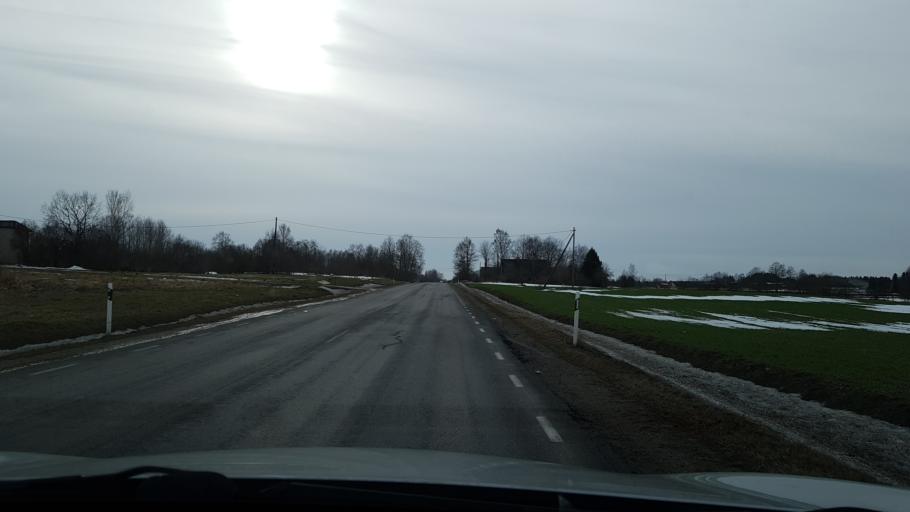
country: EE
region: Tartu
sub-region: Noo vald
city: Noo
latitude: 58.2308
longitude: 26.6445
